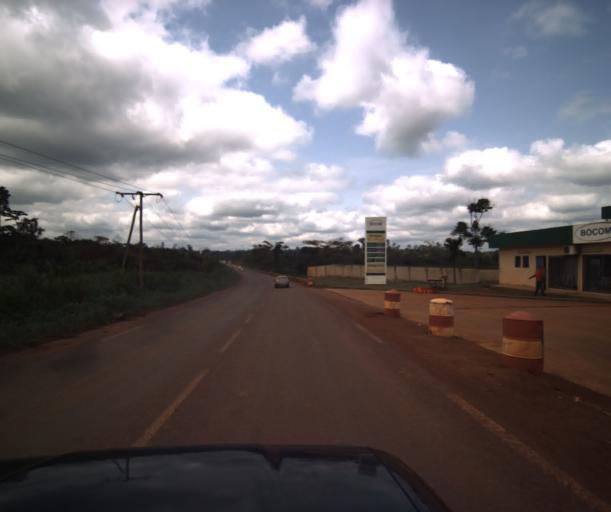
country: CM
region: Centre
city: Yaounde
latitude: 3.7931
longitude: 11.4742
